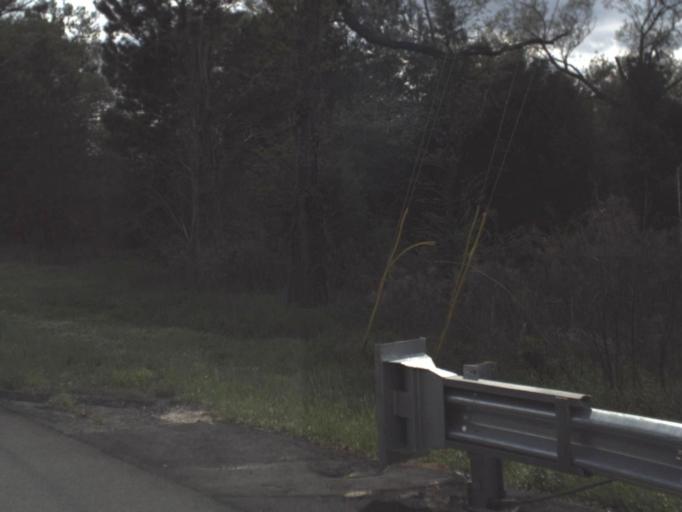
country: US
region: Florida
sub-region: Okaloosa County
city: Crestview
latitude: 30.8836
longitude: -86.5070
